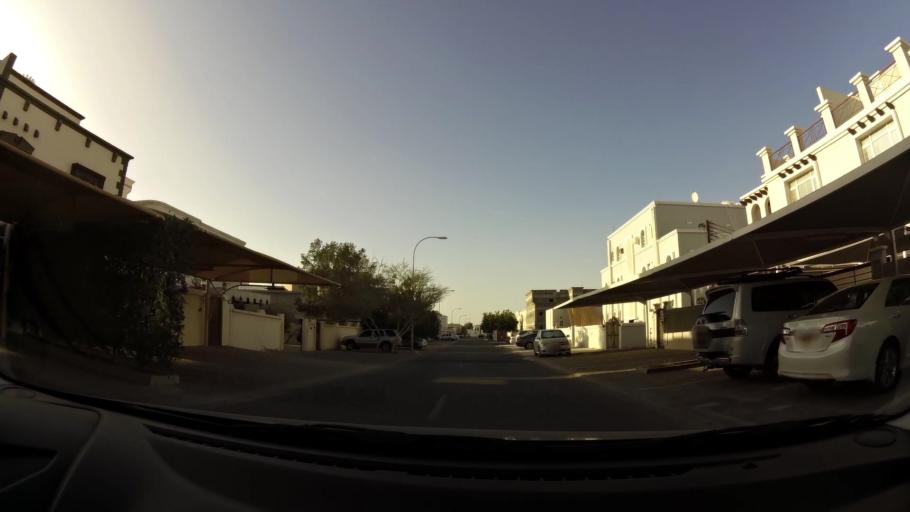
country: OM
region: Muhafazat Masqat
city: As Sib al Jadidah
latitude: 23.6101
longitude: 58.2290
